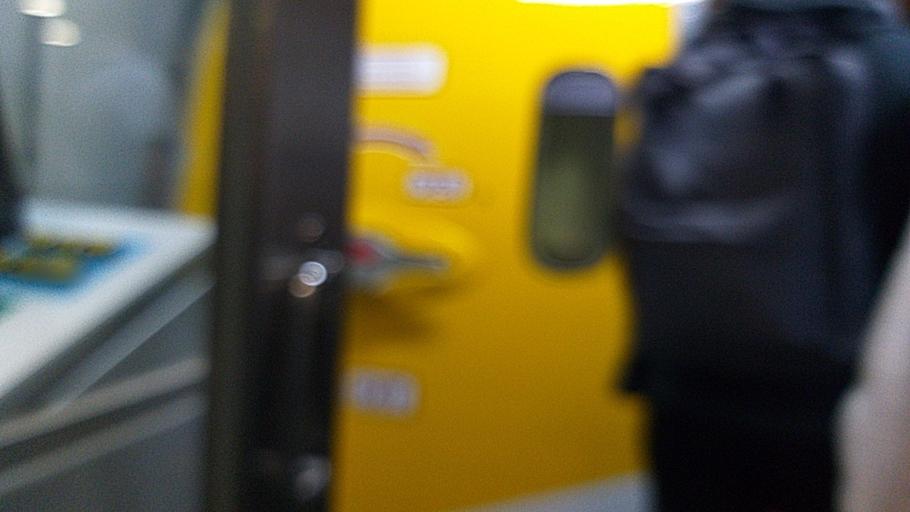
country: SG
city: Singapore
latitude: 1.3556
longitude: 103.9926
